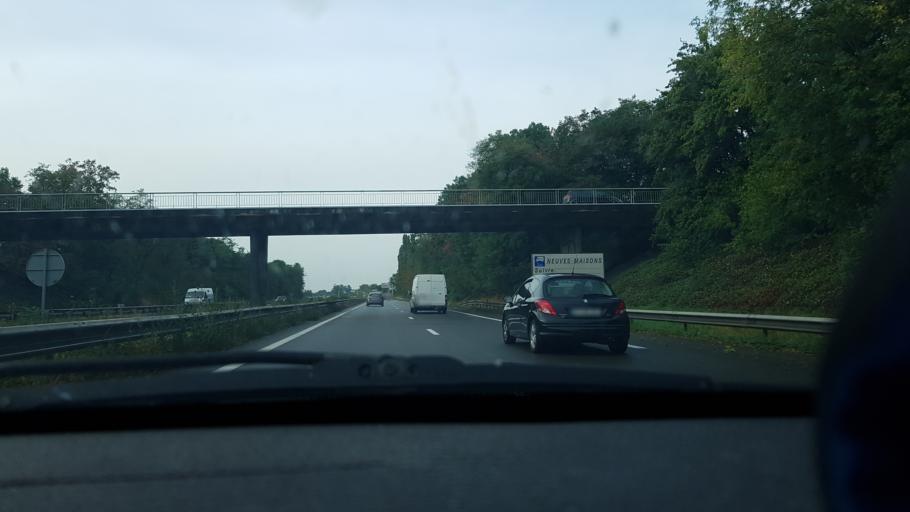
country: FR
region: Lorraine
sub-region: Departement de Meurthe-et-Moselle
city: Vandoeuvre-les-Nancy
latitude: 48.6462
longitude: 6.1813
